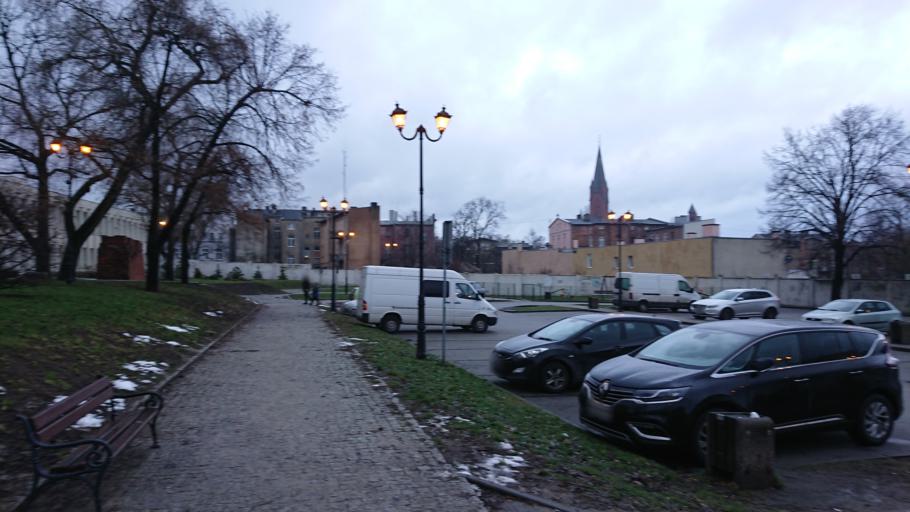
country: PL
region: Kujawsko-Pomorskie
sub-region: Powiat inowroclawski
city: Inowroclaw
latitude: 52.7972
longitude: 18.2607
